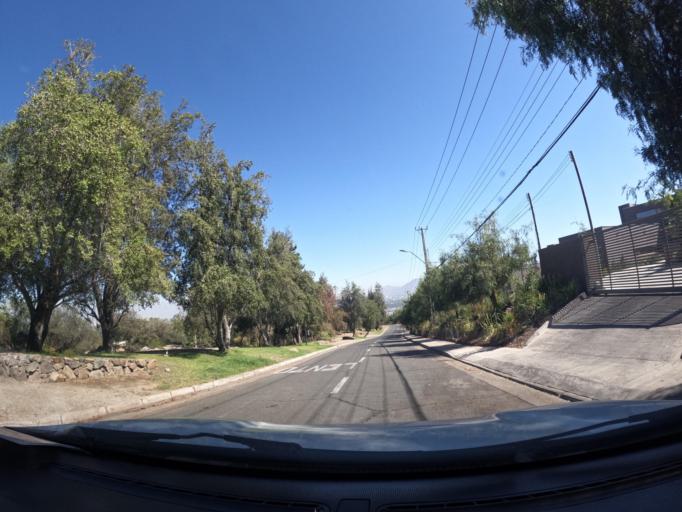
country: CL
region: Santiago Metropolitan
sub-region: Provincia de Santiago
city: Villa Presidente Frei, Nunoa, Santiago, Chile
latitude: -33.4761
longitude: -70.5197
